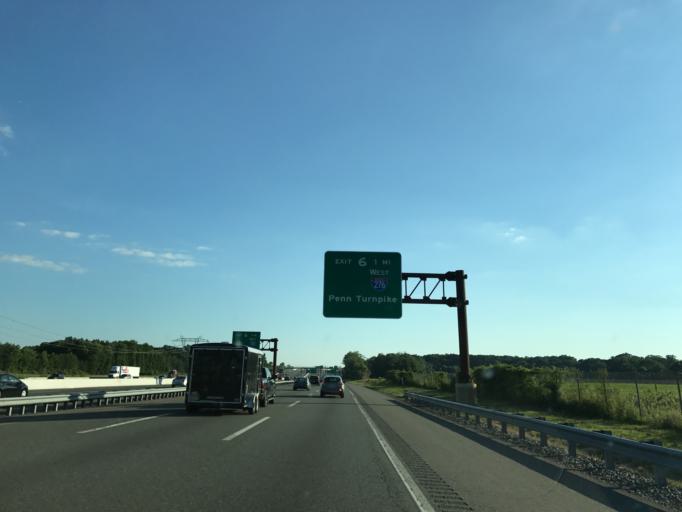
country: US
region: New Jersey
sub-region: Burlington County
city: Bordentown
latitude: 40.1124
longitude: -74.7148
